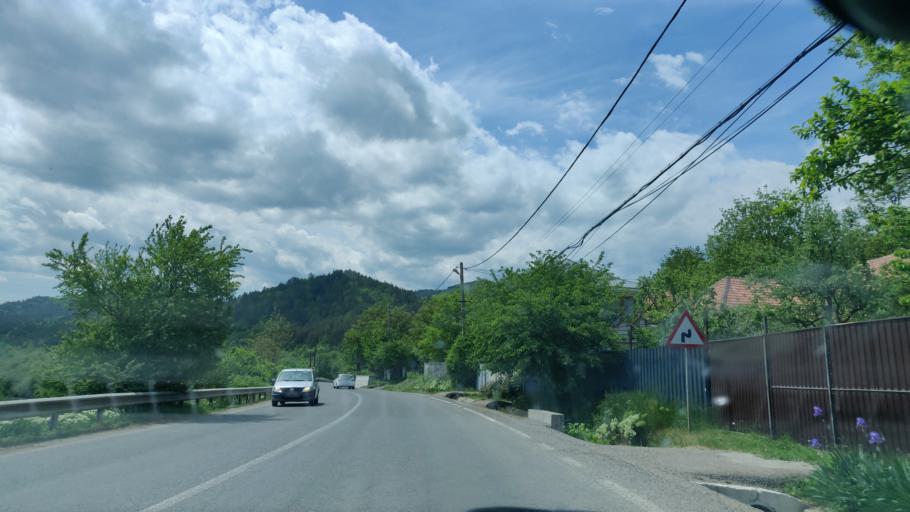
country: RO
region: Vrancea
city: Matacina
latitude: 45.8885
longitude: 26.8170
